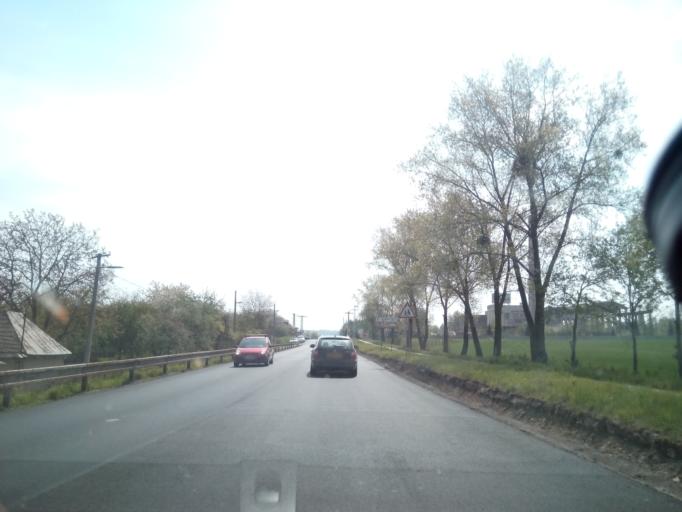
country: SK
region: Presovsky
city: Giraltovce
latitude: 49.0064
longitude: 21.5414
